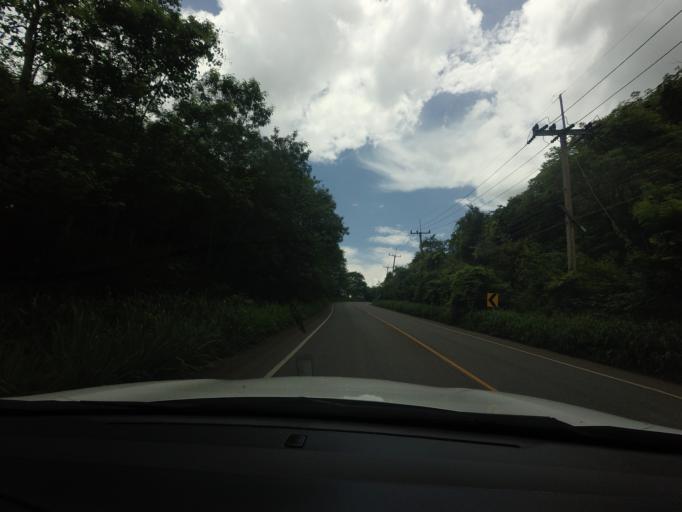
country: TH
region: Sara Buri
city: Muak Lek
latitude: 14.5582
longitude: 101.3053
